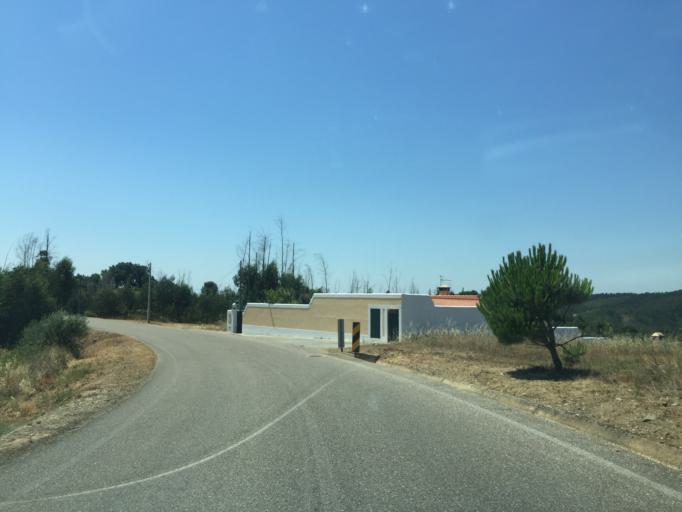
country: PT
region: Santarem
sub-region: Tomar
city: Tomar
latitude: 39.5802
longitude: -8.2976
